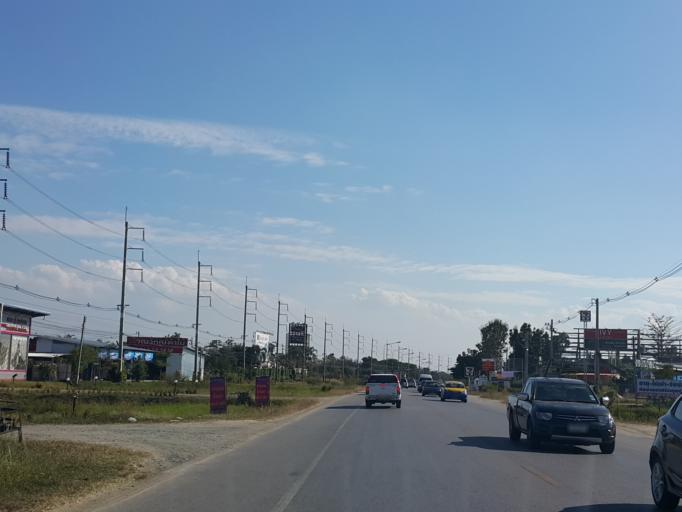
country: TH
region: Chiang Mai
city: San Sai
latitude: 18.7911
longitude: 99.0686
